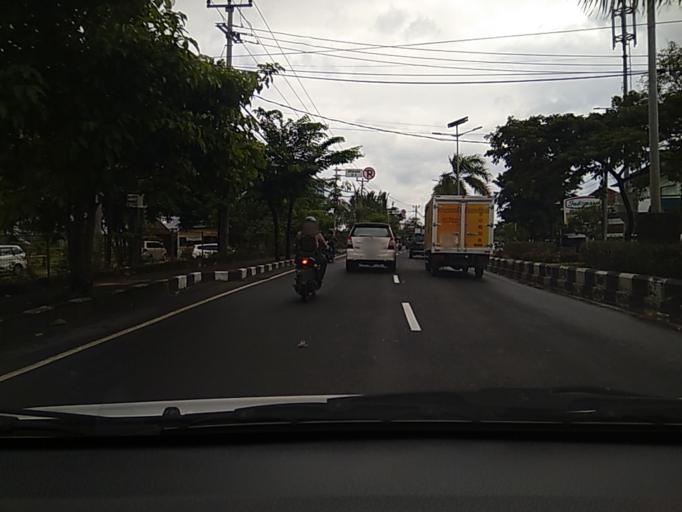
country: ID
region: Bali
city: Bualu
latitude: -8.7850
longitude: 115.1944
